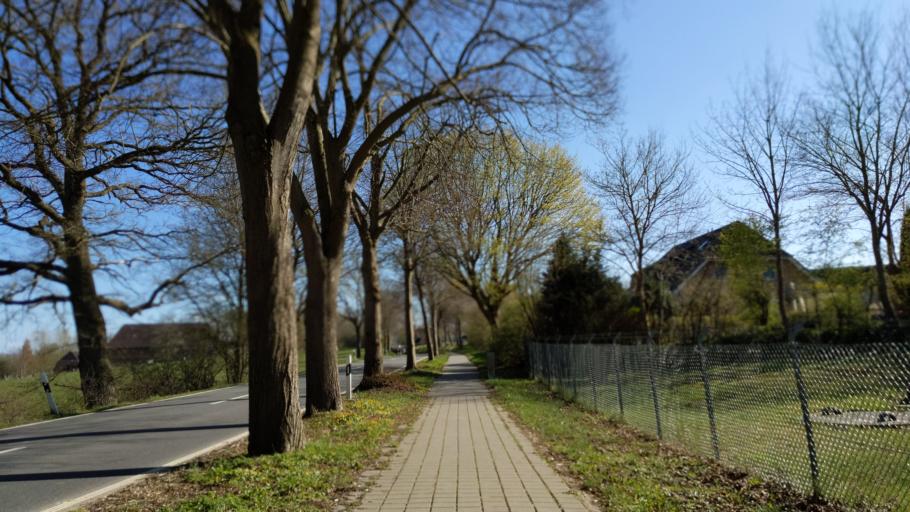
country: DE
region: Schleswig-Holstein
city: Eutin
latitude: 54.0966
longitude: 10.6130
